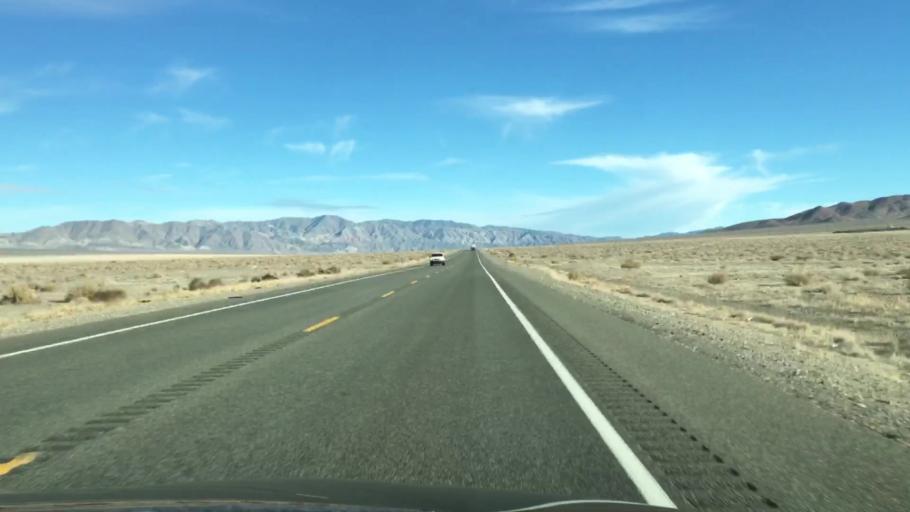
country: US
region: Nevada
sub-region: Mineral County
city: Hawthorne
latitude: 38.5371
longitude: -118.3362
